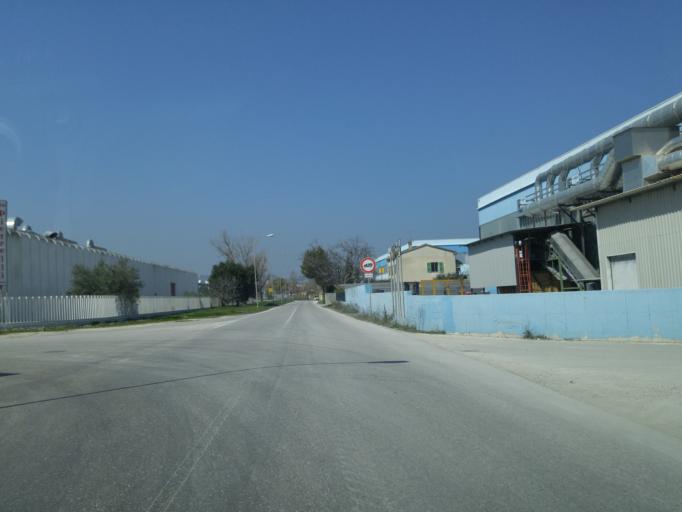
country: IT
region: The Marches
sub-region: Provincia di Pesaro e Urbino
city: Bellocchi
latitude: 43.7886
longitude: 13.0108
